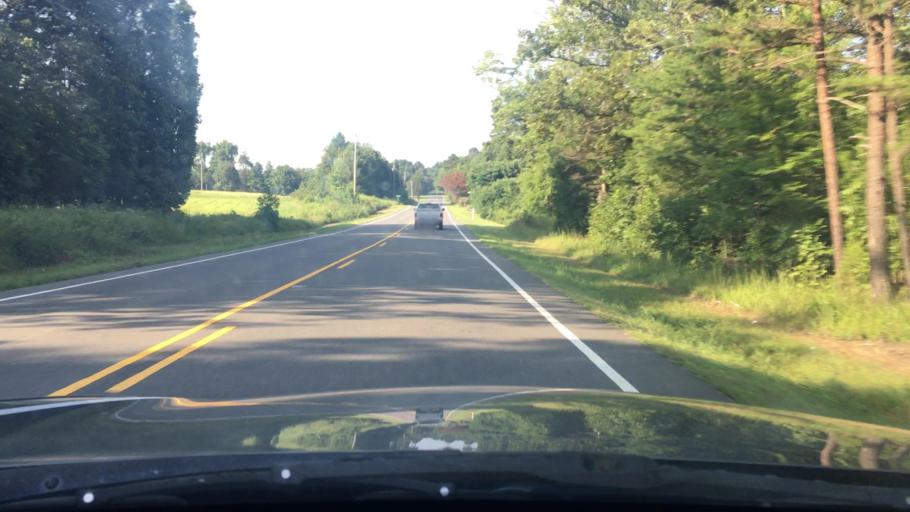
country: US
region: North Carolina
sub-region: Caswell County
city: Yanceyville
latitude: 36.3008
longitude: -79.3651
